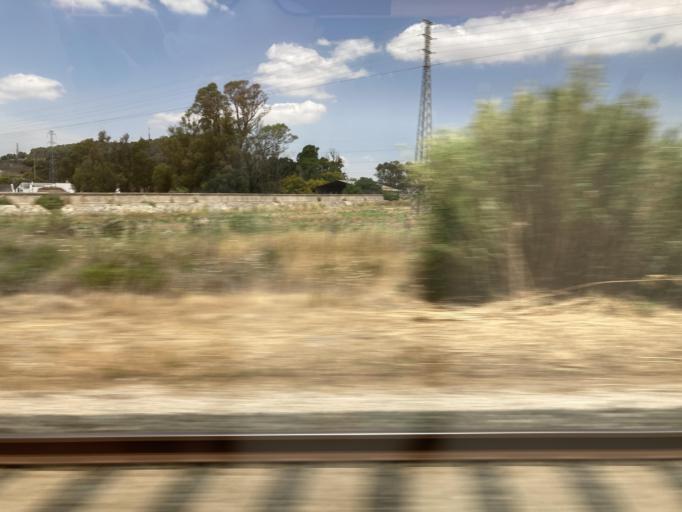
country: ES
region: Andalusia
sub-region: Provincia de Cadiz
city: Jerez de la Frontera
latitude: 36.6216
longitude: -6.1432
